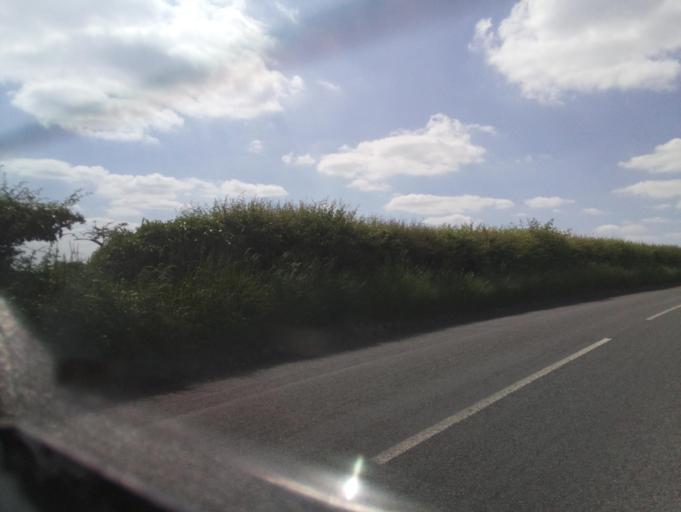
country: GB
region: England
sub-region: Wiltshire
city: Woodborough
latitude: 51.3622
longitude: -1.8624
